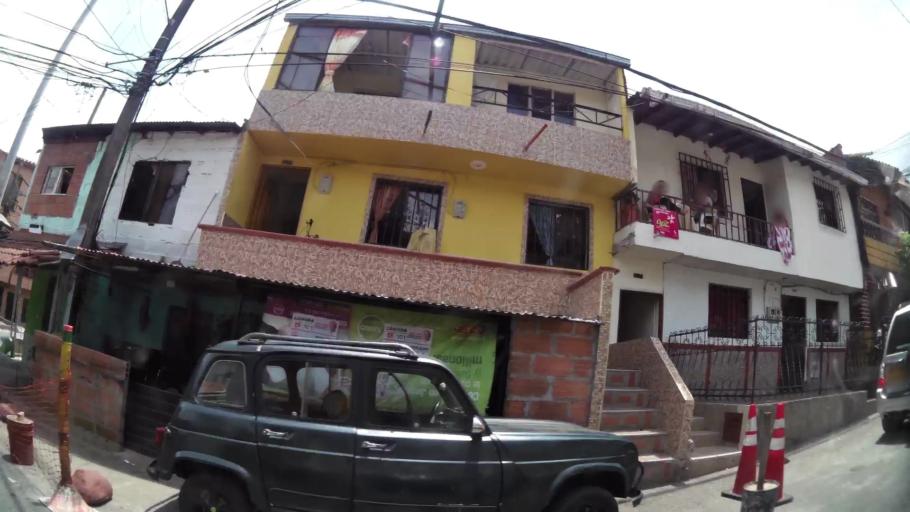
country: CO
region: Antioquia
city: Bello
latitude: 6.3369
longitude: -75.5524
